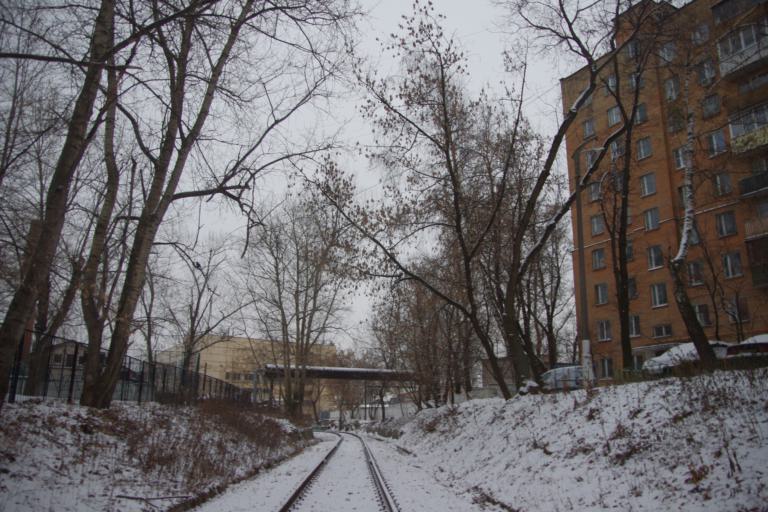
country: RU
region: Moscow
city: Nagornyy
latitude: 55.6597
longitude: 37.6260
